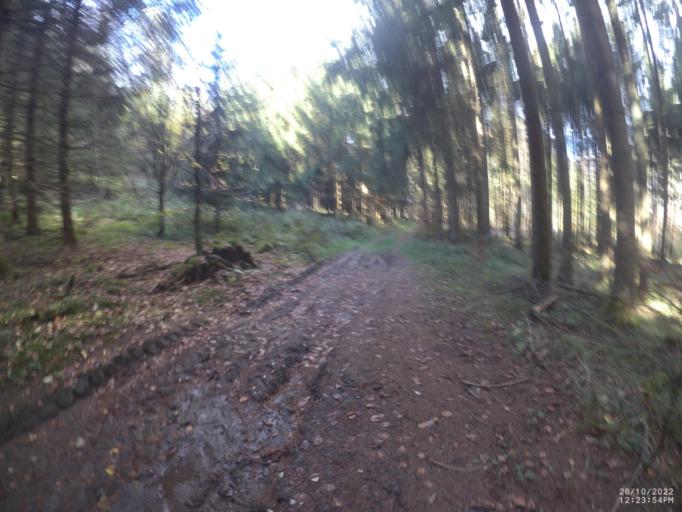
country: DE
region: Baden-Wuerttemberg
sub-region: Regierungsbezirk Stuttgart
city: Wiesensteig
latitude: 48.5417
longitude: 9.6127
